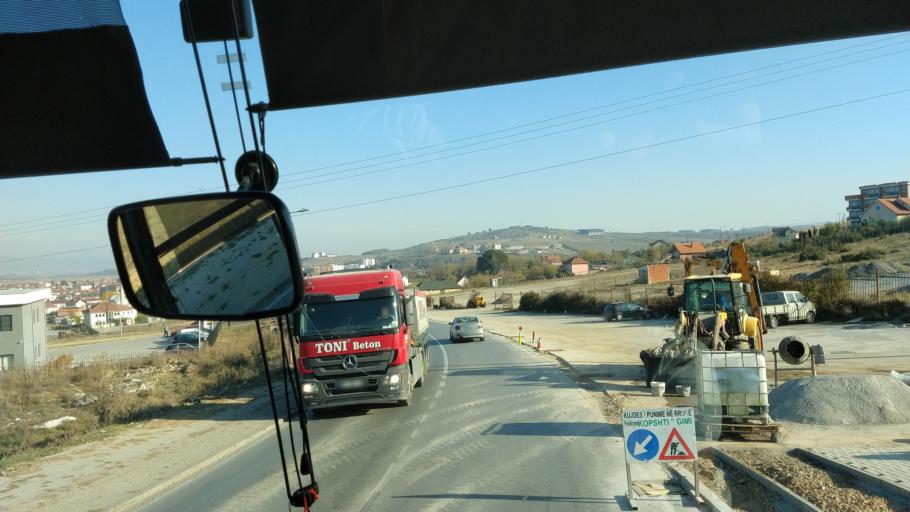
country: XK
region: Ferizaj
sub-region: Komuna e Shtimes
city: Shtime
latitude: 42.4362
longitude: 21.0243
